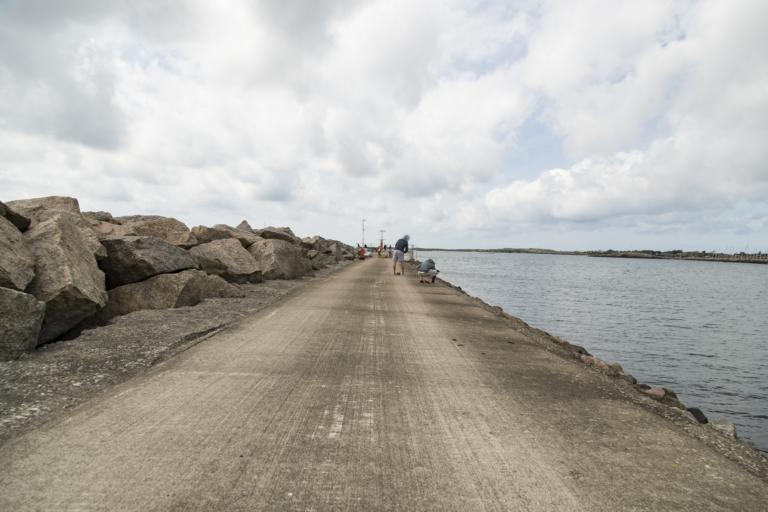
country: SE
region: Halland
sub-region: Varbergs Kommun
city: Varberg
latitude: 57.1079
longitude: 12.2350
